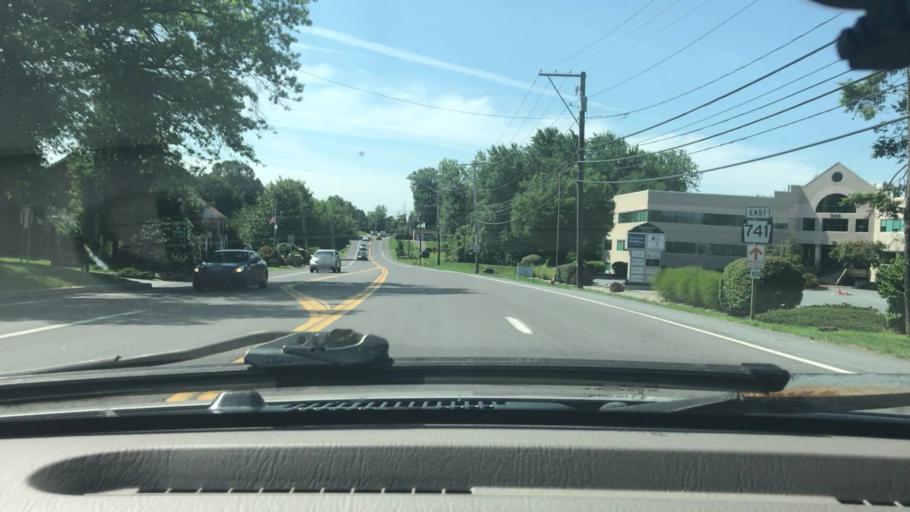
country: US
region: Pennsylvania
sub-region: Lancaster County
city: East Petersburg
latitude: 40.0590
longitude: -76.3600
